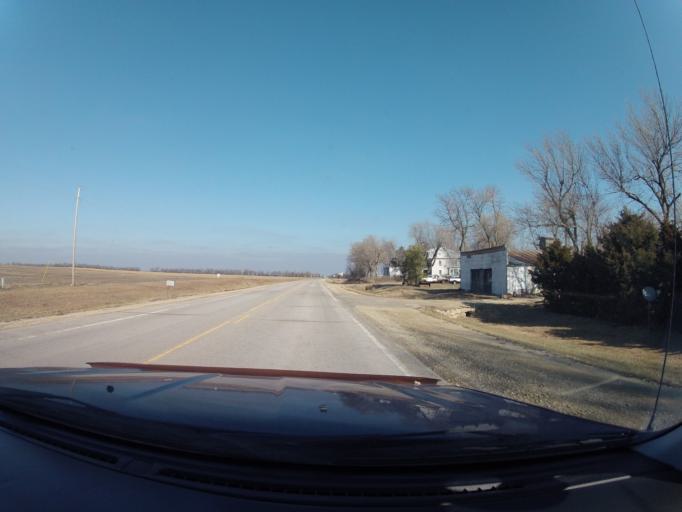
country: US
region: Kansas
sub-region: Marshall County
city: Blue Rapids
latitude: 39.5969
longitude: -96.7501
